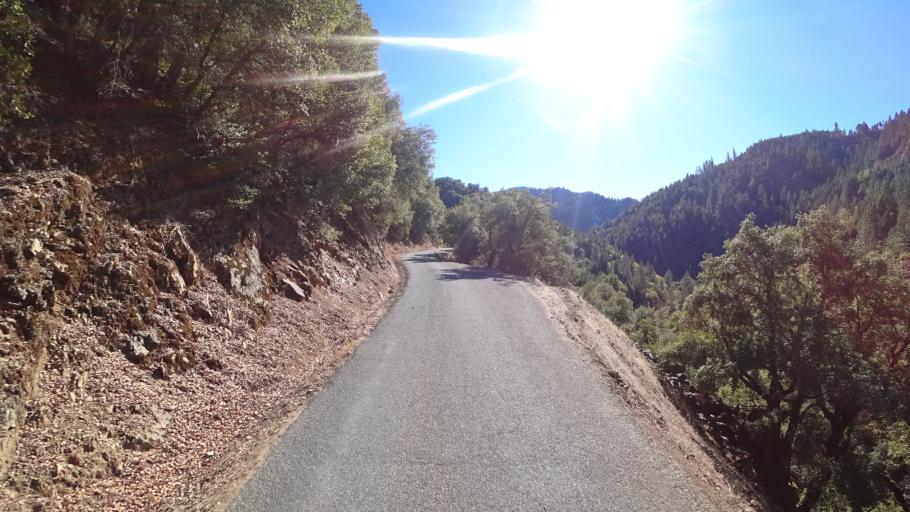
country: US
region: California
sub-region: Humboldt County
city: Willow Creek
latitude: 41.1687
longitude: -123.2171
